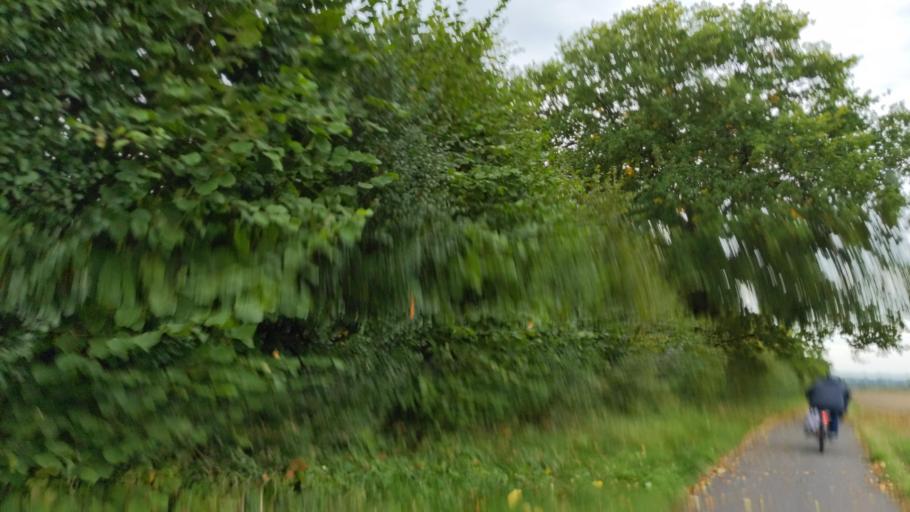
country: DE
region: Schleswig-Holstein
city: Buchholz
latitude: 53.7640
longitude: 10.7814
